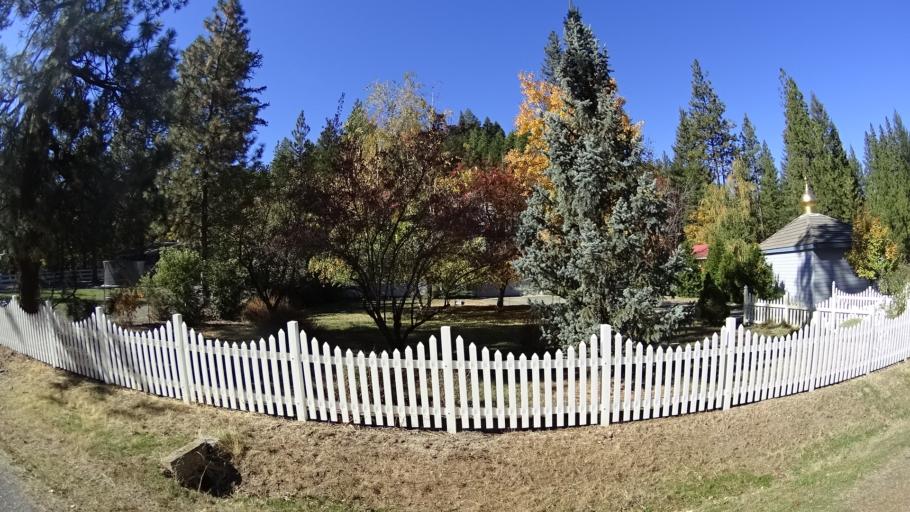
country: US
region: California
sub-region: Siskiyou County
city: Yreka
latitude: 41.5197
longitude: -122.9229
